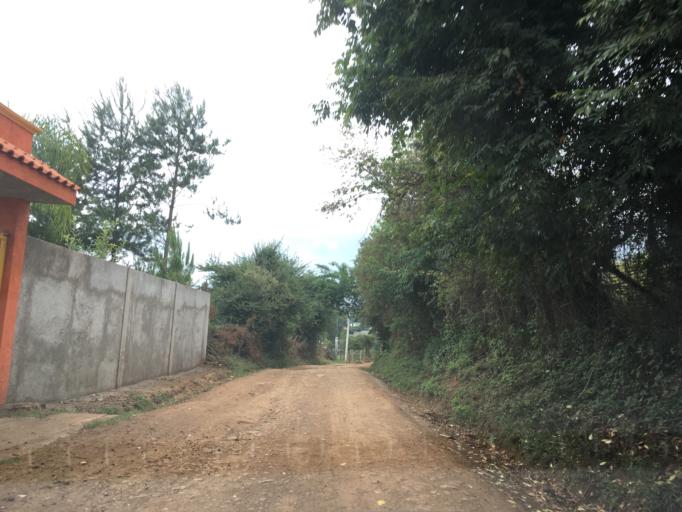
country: MX
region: Michoacan
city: Acuitzio del Canje
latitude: 19.5034
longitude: -101.2185
